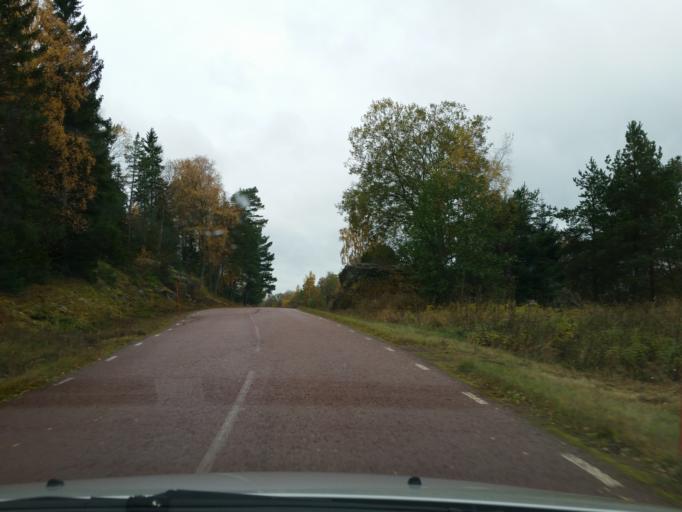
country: AX
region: Alands landsbygd
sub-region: Lumparland
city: Lumparland
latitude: 60.1450
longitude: 20.2728
